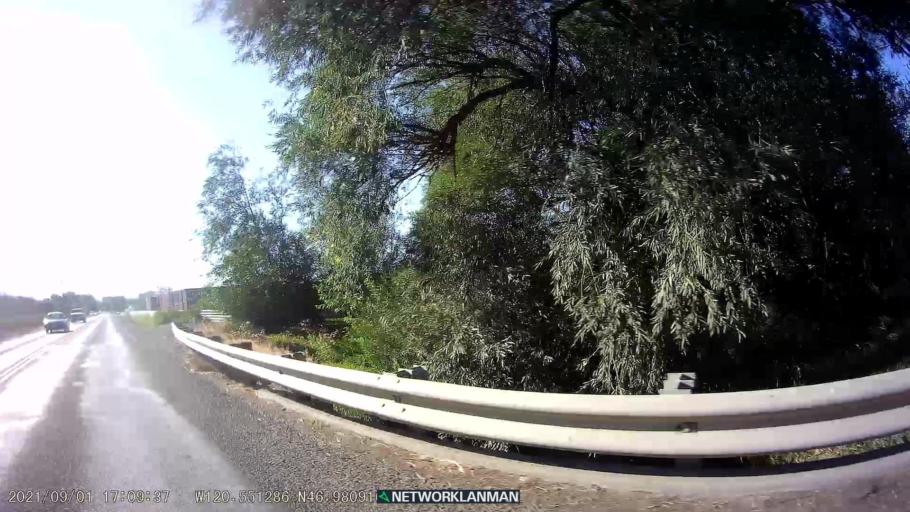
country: US
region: Washington
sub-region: Kittitas County
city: Ellensburg
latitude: 46.9809
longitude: -120.5515
